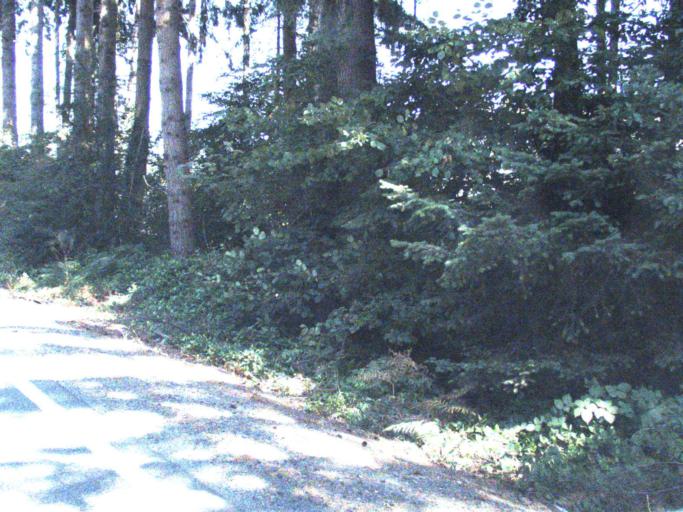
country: US
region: Washington
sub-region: Snohomish County
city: Martha Lake
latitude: 47.8206
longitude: -122.2327
